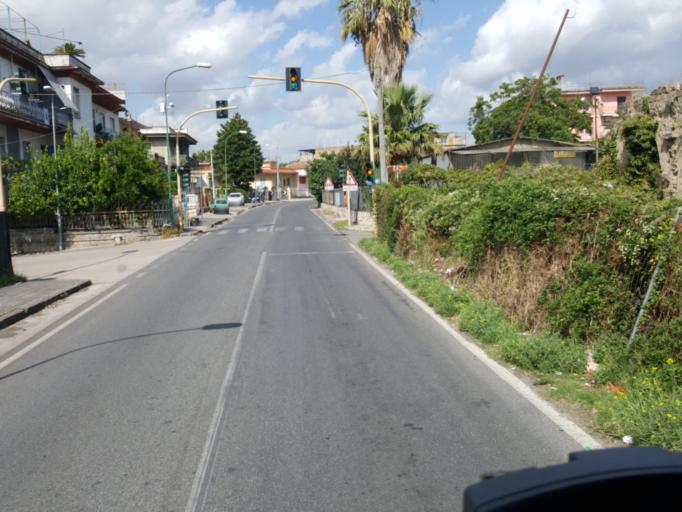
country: IT
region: Campania
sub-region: Provincia di Napoli
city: Liveri
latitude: 40.9038
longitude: 14.5639
